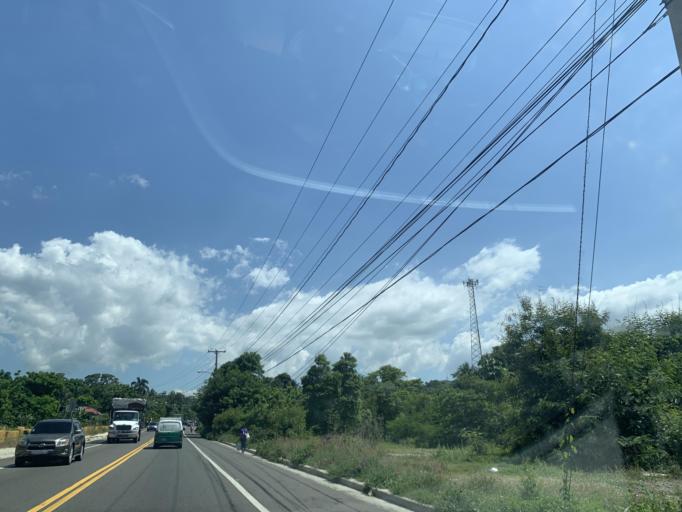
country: DO
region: Puerto Plata
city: Imbert
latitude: 19.7193
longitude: -70.8337
